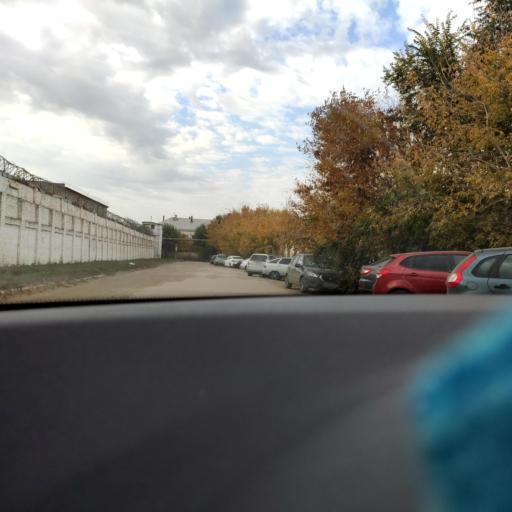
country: RU
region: Samara
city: Samara
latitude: 53.1942
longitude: 50.2645
